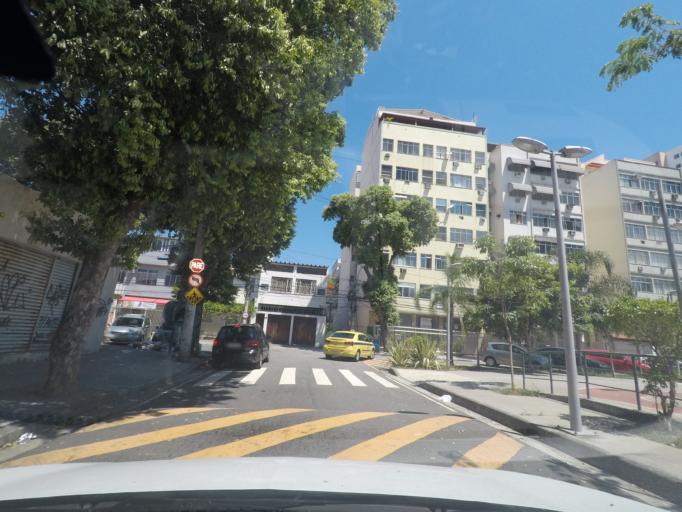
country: BR
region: Rio de Janeiro
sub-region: Rio De Janeiro
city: Rio de Janeiro
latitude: -22.9159
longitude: -43.2341
